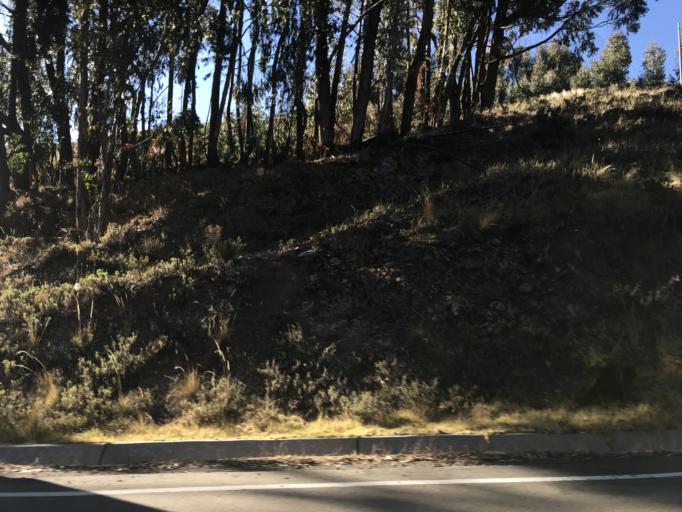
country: BO
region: La Paz
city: San Pedro
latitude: -16.2259
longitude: -68.8512
